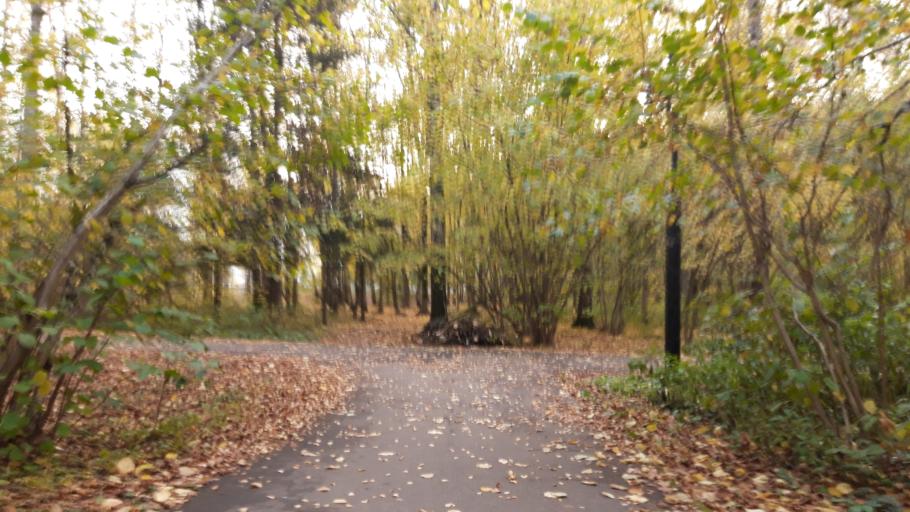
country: RU
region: Moscow
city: Zelenograd
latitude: 55.9973
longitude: 37.1962
